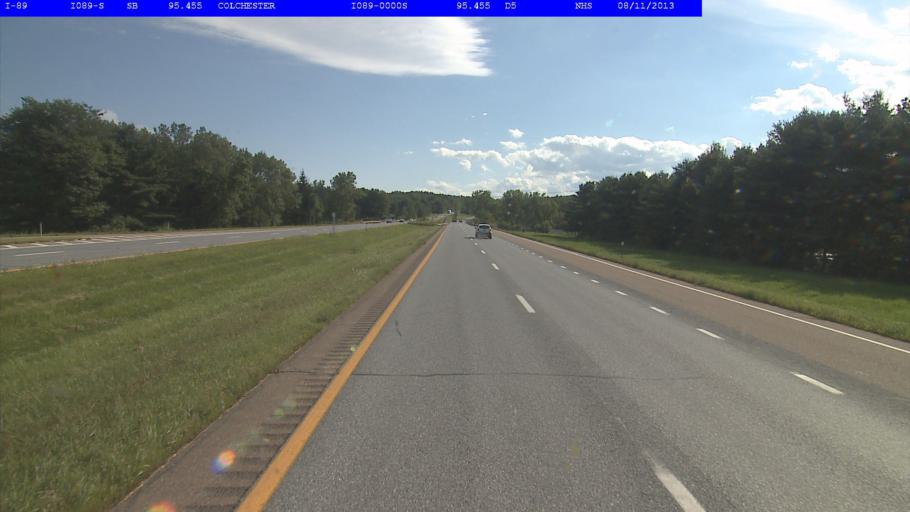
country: US
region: Vermont
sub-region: Chittenden County
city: Colchester
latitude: 44.5564
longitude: -73.1835
